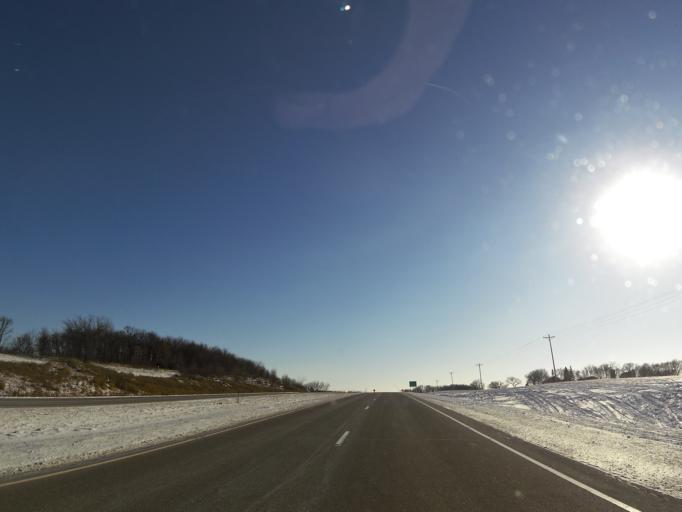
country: US
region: Minnesota
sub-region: Le Sueur County
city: New Prague
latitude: 44.5506
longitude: -93.5019
